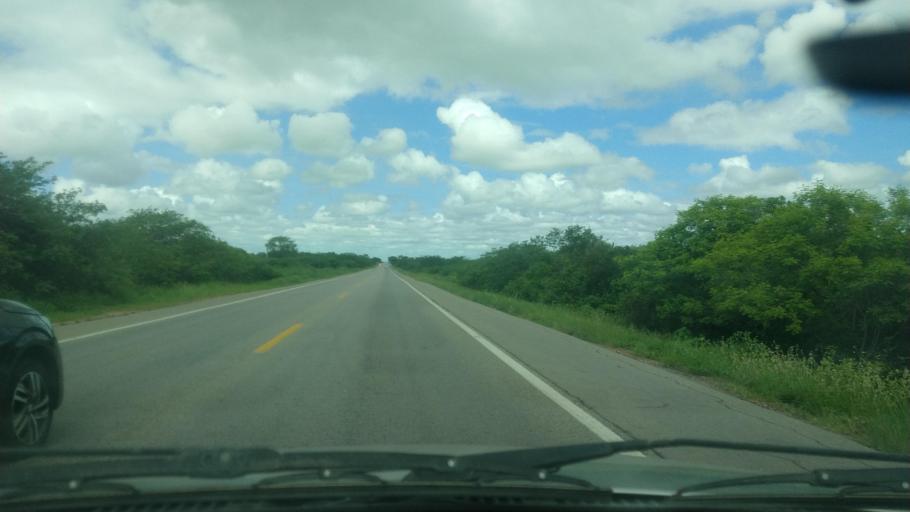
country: BR
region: Rio Grande do Norte
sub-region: Tangara
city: Tangara
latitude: -6.1648
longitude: -35.7566
